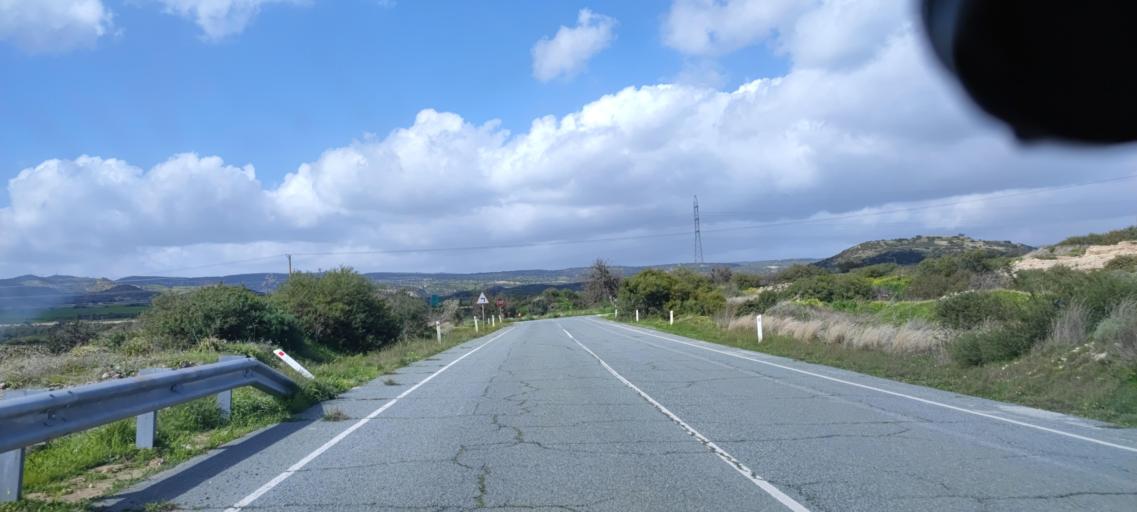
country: CY
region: Limassol
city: Pissouri
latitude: 34.6820
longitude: 32.7488
